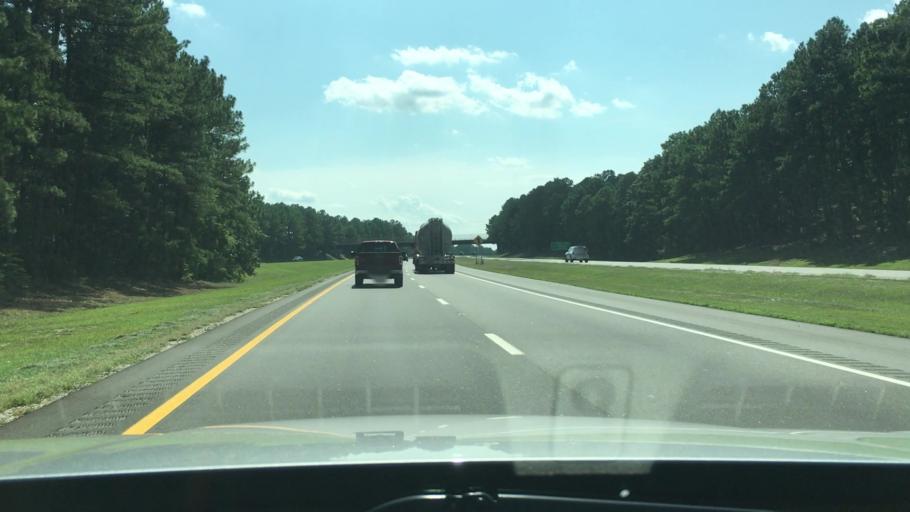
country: US
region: North Carolina
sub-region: Cumberland County
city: Fayetteville
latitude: 34.9747
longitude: -78.8610
